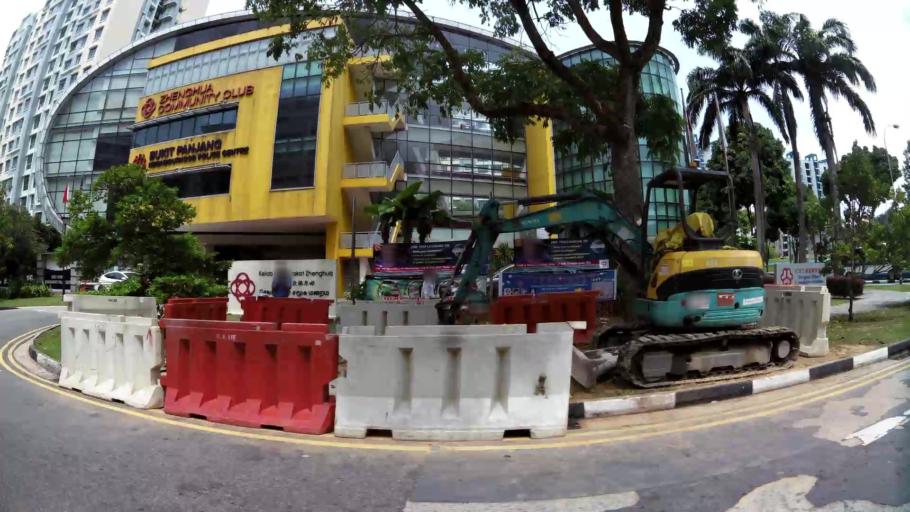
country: MY
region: Johor
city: Johor Bahru
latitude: 1.3864
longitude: 103.7717
